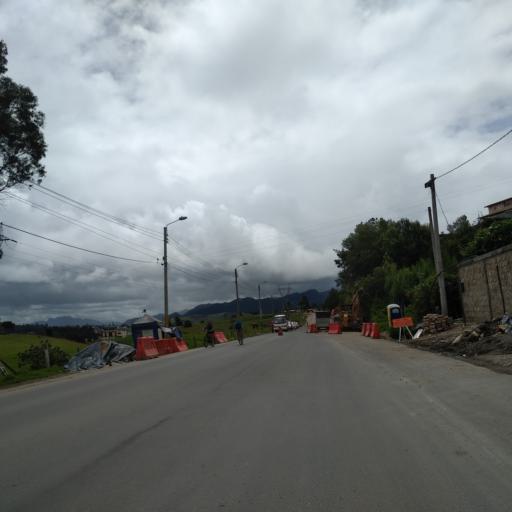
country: CO
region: Cundinamarca
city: La Calera
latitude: 4.7021
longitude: -73.9804
